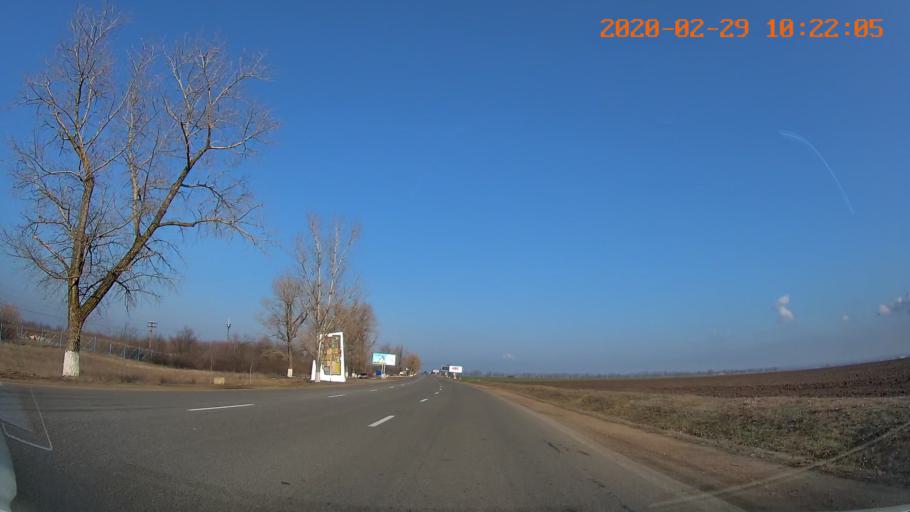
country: MD
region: Telenesti
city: Tiraspolul Nou
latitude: 46.8722
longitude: 29.6080
